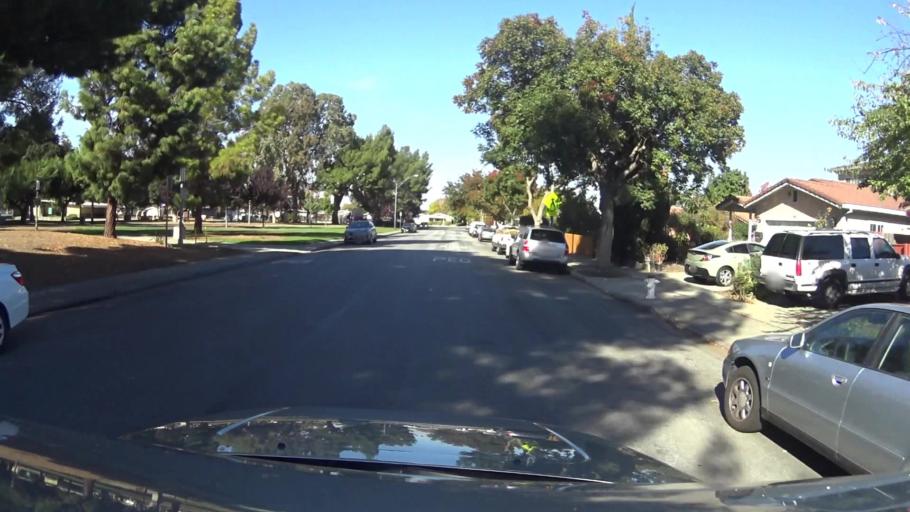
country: US
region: California
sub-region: Santa Clara County
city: Sunnyvale
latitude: 37.3970
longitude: -121.9991
